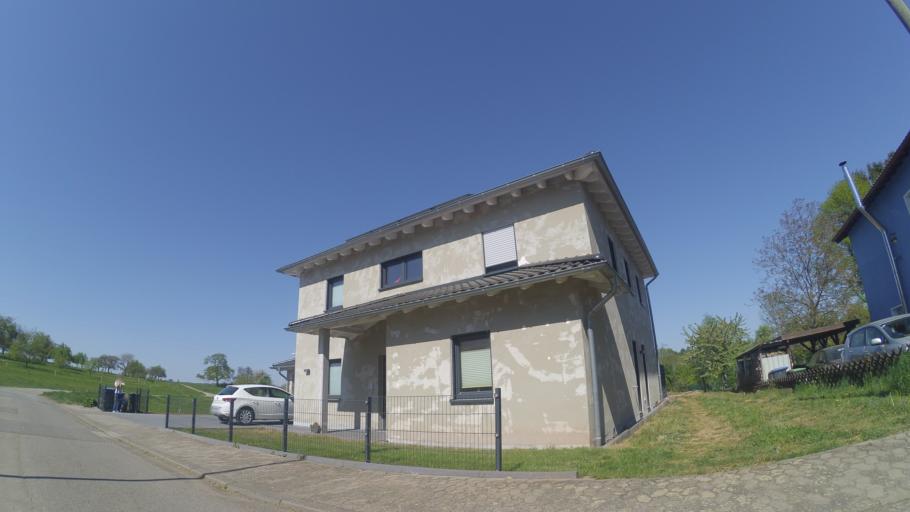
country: DE
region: Saarland
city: Hangard
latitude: 49.4077
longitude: 7.2056
